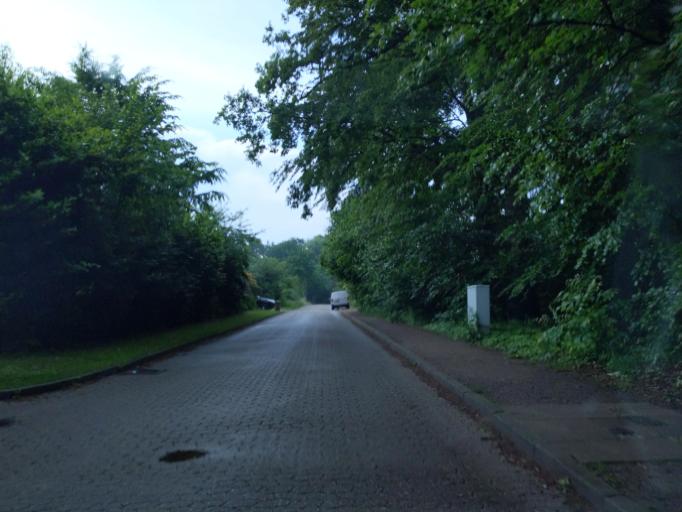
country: DE
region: Lower Saxony
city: Walsrode
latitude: 52.8732
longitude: 9.5937
